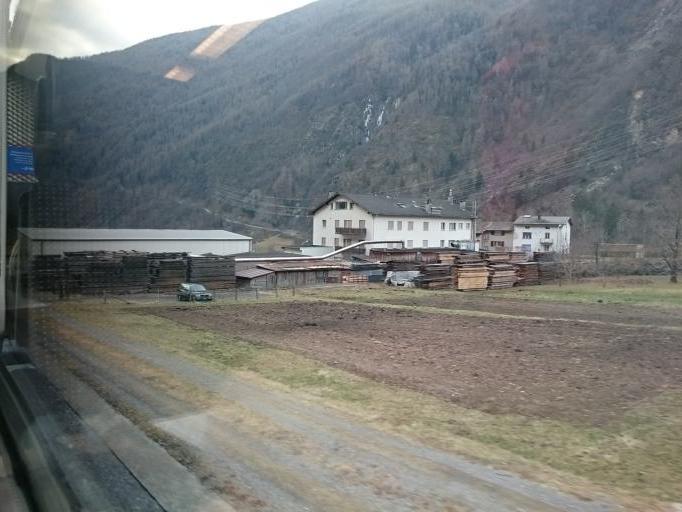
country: CH
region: Grisons
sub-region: Bernina District
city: Brusio
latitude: 46.2509
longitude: 10.1293
